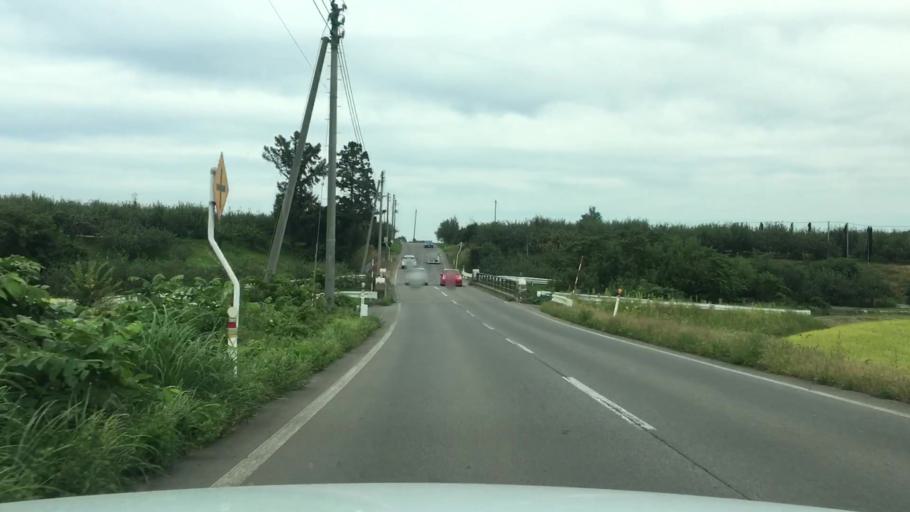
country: JP
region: Aomori
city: Hirosaki
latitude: 40.6553
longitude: 140.4207
